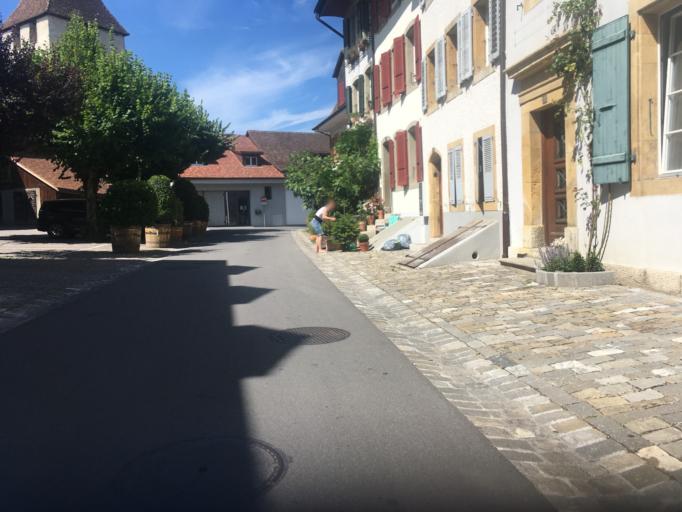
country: CH
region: Fribourg
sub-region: See District
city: Murten
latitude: 46.9277
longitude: 7.1173
